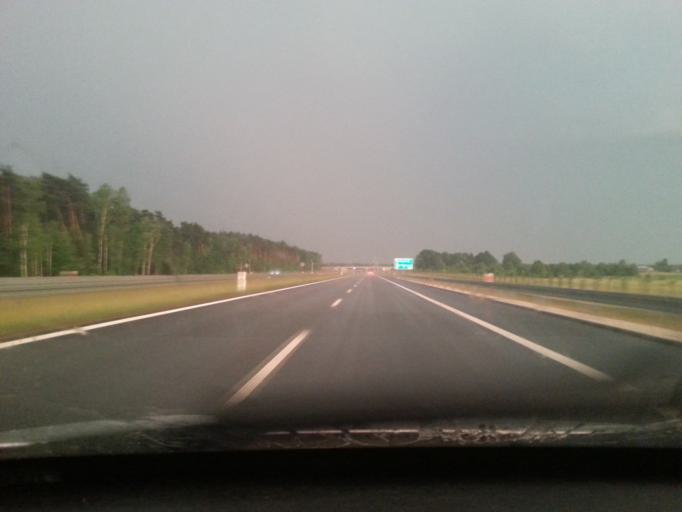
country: PL
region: Lodz Voivodeship
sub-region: Powiat pabianicki
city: Dobron
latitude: 51.6126
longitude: 19.2748
